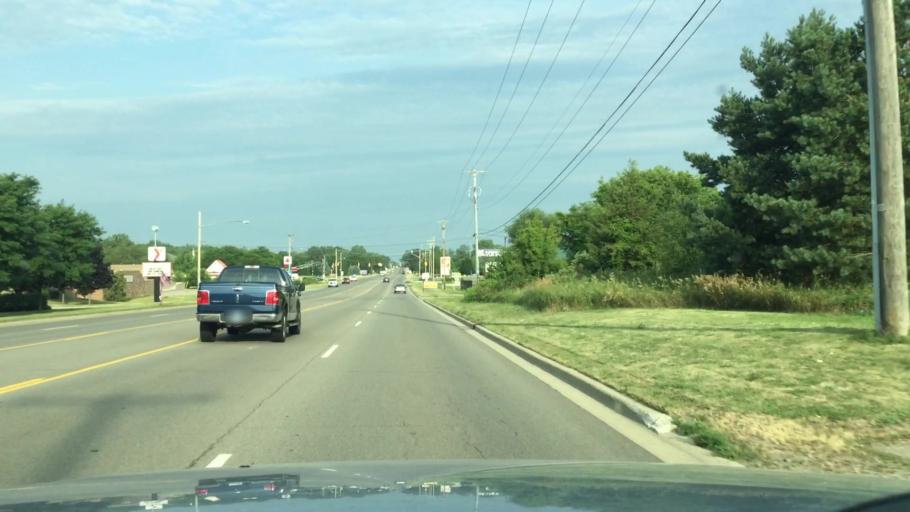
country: US
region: Michigan
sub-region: Genesee County
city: Flushing
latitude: 43.0606
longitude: -83.7795
